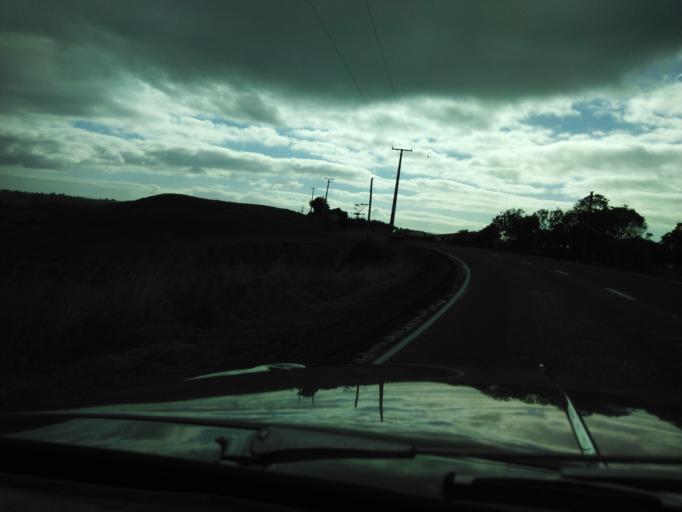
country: NZ
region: Auckland
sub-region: Auckland
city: Wellsford
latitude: -36.3062
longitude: 174.4248
